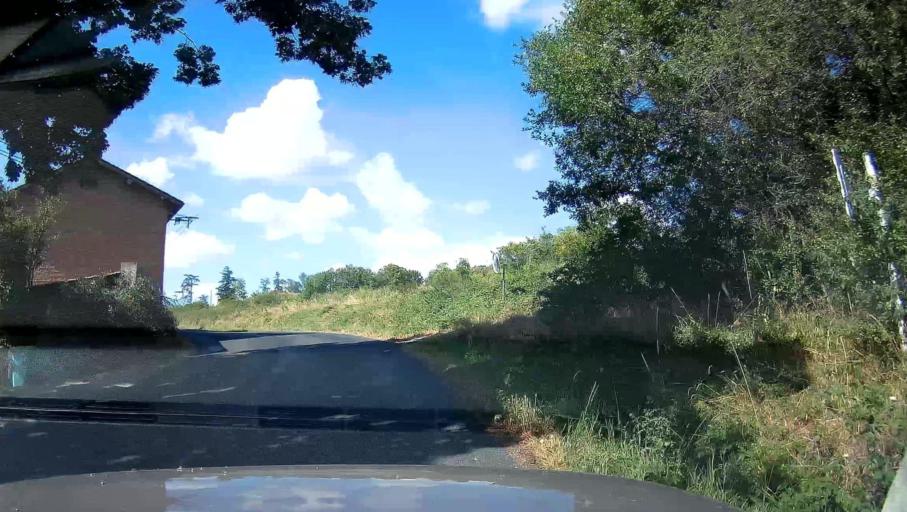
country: FR
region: Rhone-Alpes
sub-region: Departement du Rhone
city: Pommiers
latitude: 45.9509
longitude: 4.7065
